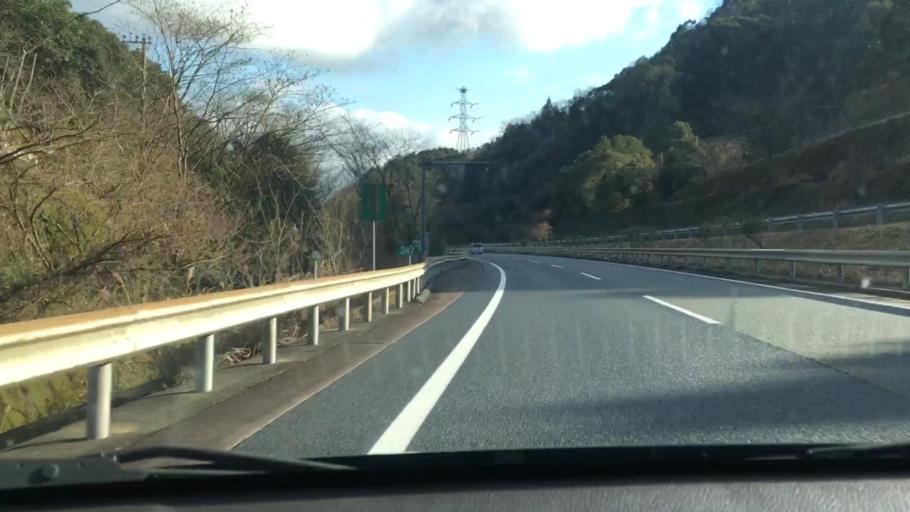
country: JP
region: Kumamoto
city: Hitoyoshi
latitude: 32.2689
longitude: 130.7611
